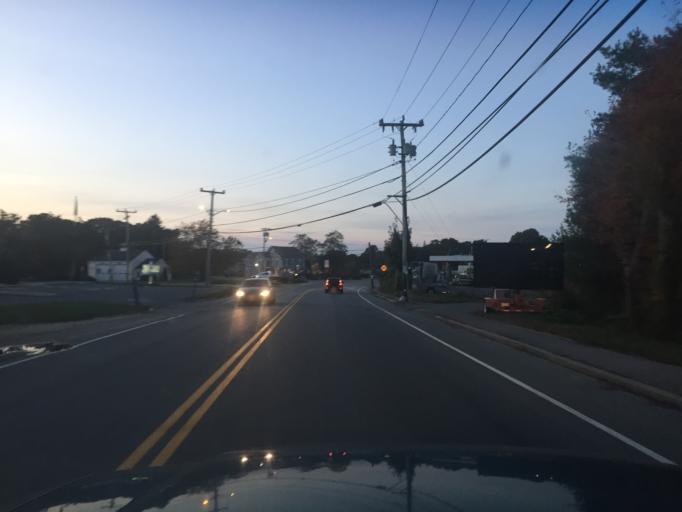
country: US
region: Massachusetts
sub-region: Plymouth County
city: Onset
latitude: 41.7556
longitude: -70.6763
